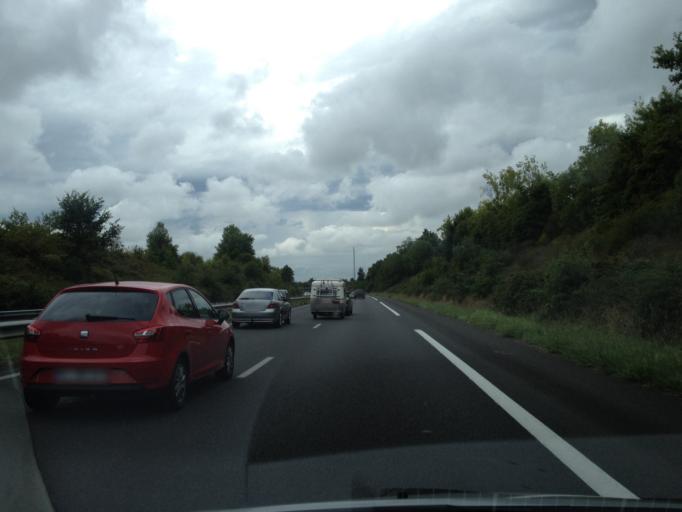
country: FR
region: Aquitaine
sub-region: Departement du Lot-et-Garonne
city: Meilhan-sur-Garonne
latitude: 44.4893
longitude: 0.0034
